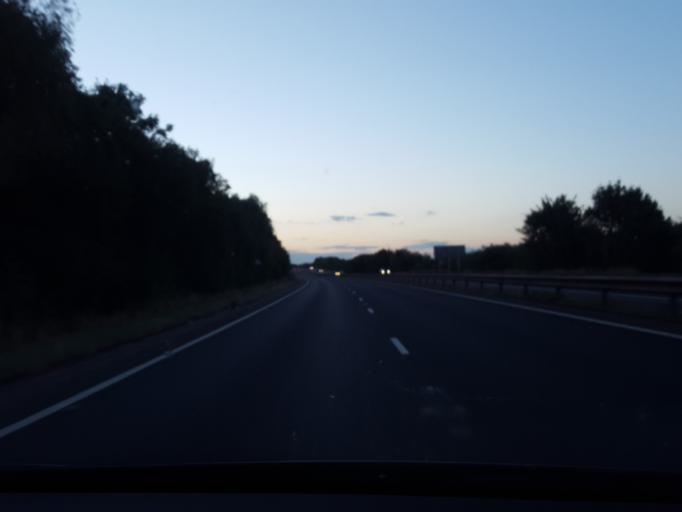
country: GB
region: England
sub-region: Leicestershire
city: Mountsorrel
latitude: 52.7270
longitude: -1.1300
